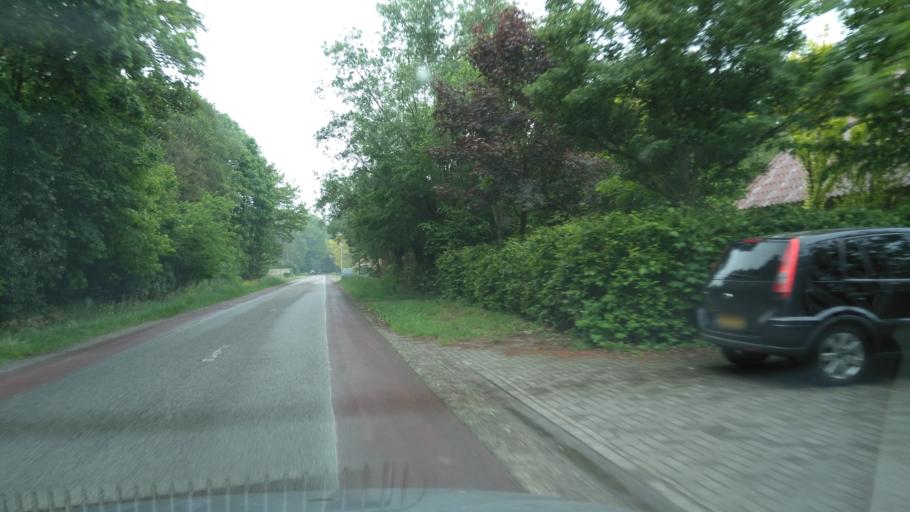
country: BE
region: Flanders
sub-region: Provincie Antwerpen
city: Baarle-Hertog
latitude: 51.3903
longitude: 4.8908
